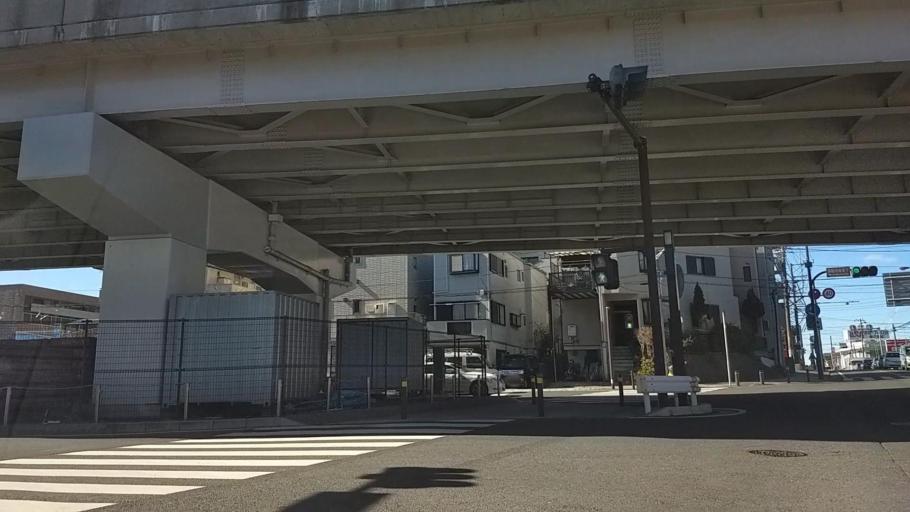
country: JP
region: Kanagawa
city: Fujisawa
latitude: 35.3403
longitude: 139.5027
